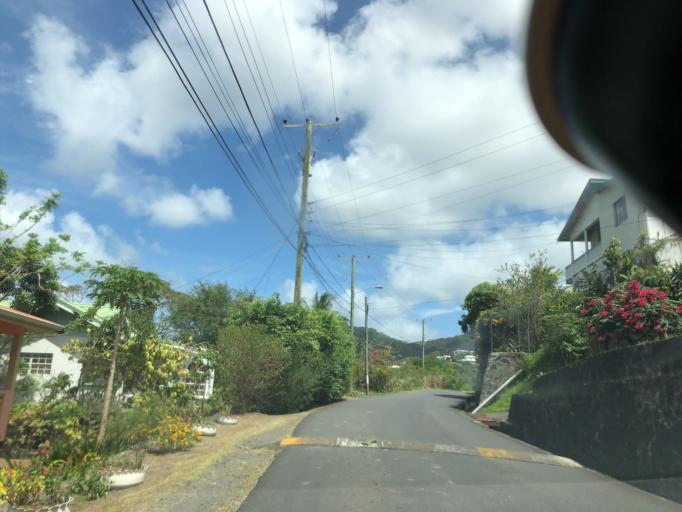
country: LC
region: Gros-Islet
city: Gros Islet
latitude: 14.0626
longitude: -60.9681
